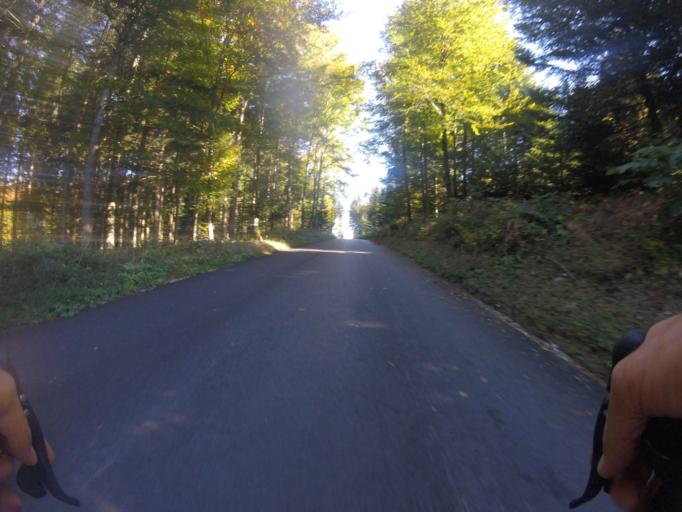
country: CH
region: Bern
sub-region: Bern-Mittelland District
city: Kirchlindach
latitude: 47.0133
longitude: 7.4025
